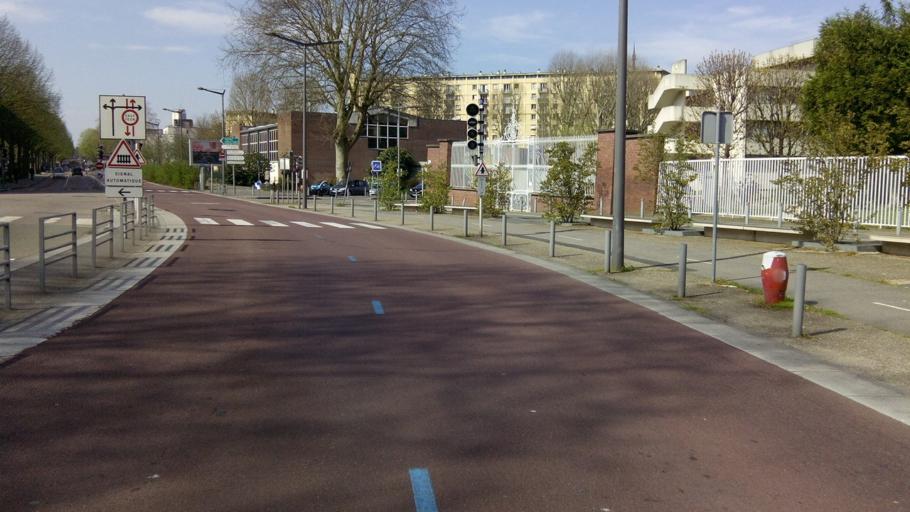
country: FR
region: Haute-Normandie
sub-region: Departement de la Seine-Maritime
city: Rouen
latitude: 49.4389
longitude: 1.1085
